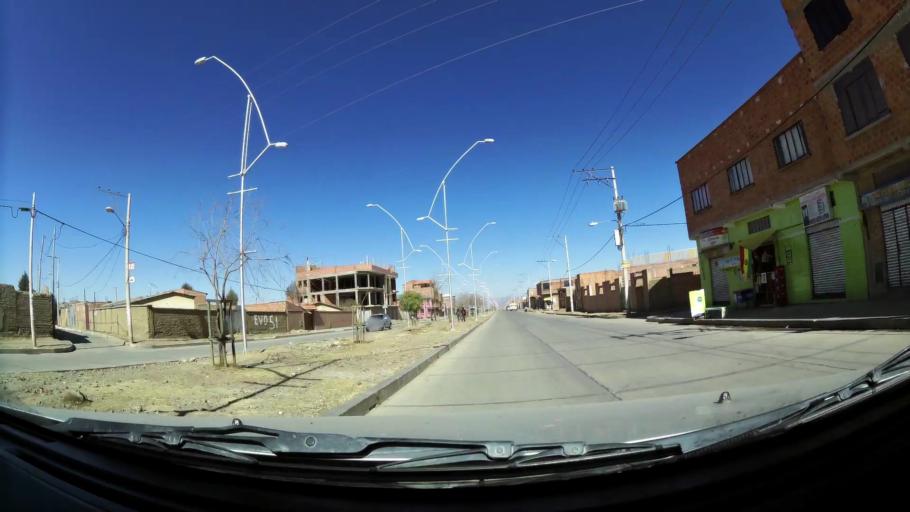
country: BO
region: La Paz
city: La Paz
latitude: -16.5288
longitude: -68.2304
